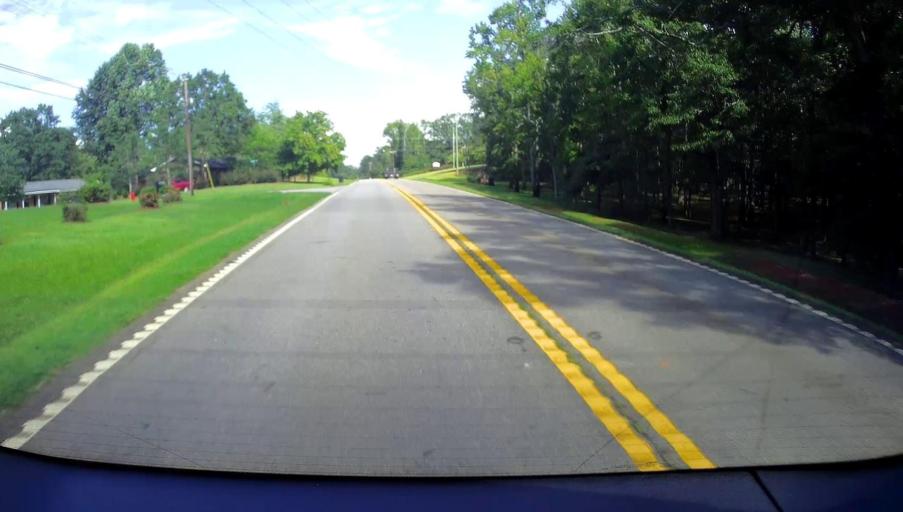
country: US
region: Georgia
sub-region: Upson County
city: Thomaston
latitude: 32.8764
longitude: -84.3451
